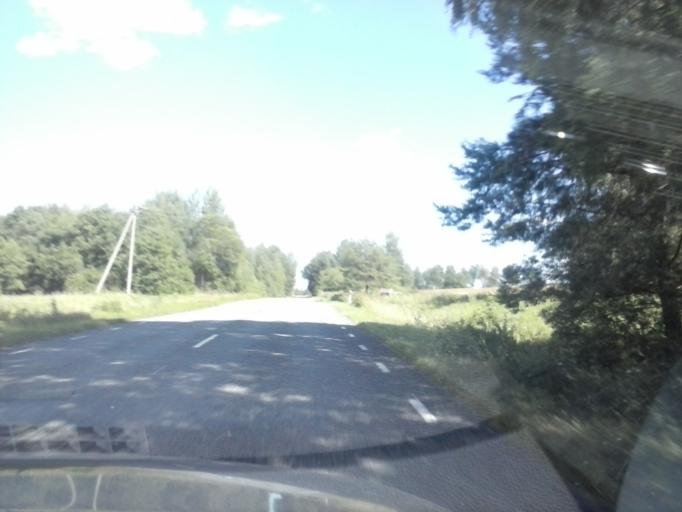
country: LV
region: Apes Novads
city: Ape
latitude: 57.7295
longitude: 26.8136
